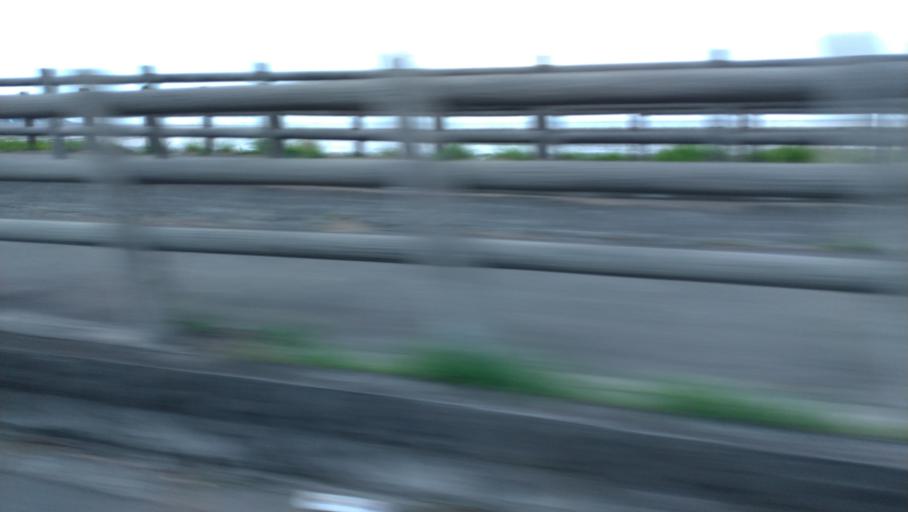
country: TW
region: Taiwan
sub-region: Hsinchu
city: Hsinchu
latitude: 24.7546
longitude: 120.9058
